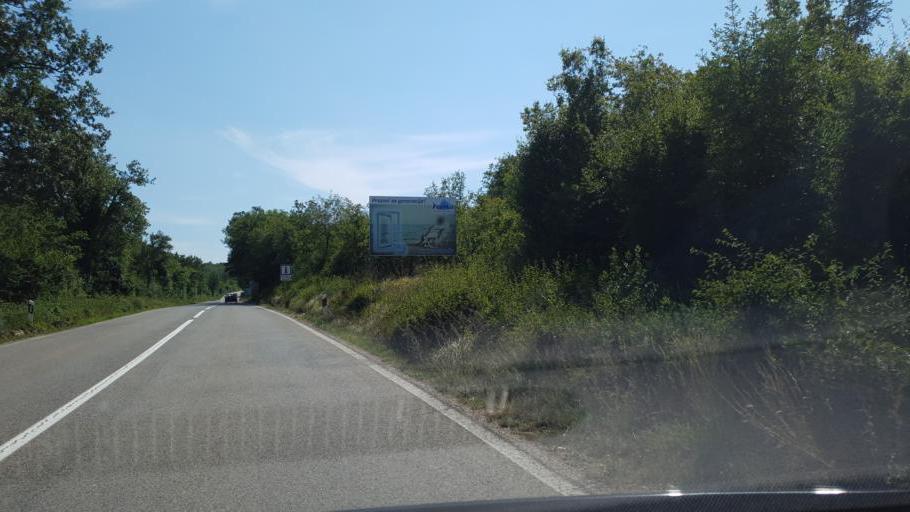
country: HR
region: Primorsko-Goranska
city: Njivice
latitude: 45.1674
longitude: 14.5528
